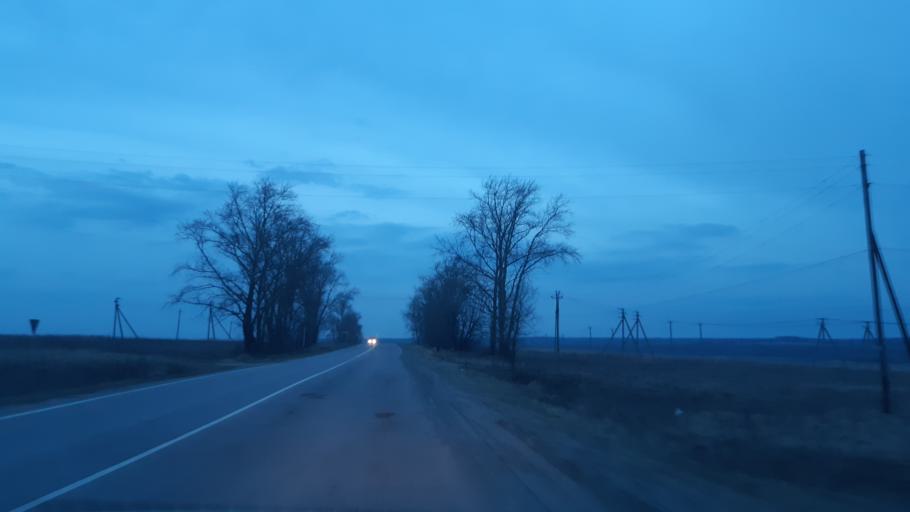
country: RU
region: Vladimir
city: Nikologory
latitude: 56.1623
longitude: 41.9959
